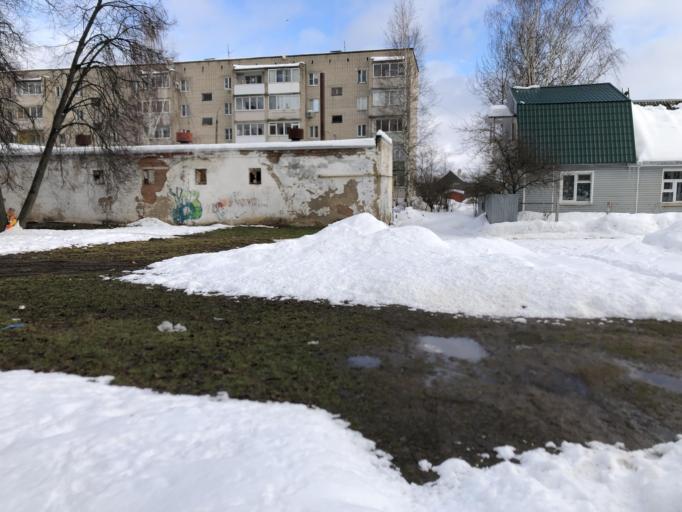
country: RU
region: Smolensk
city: Safonovo
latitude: 55.1144
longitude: 33.2425
